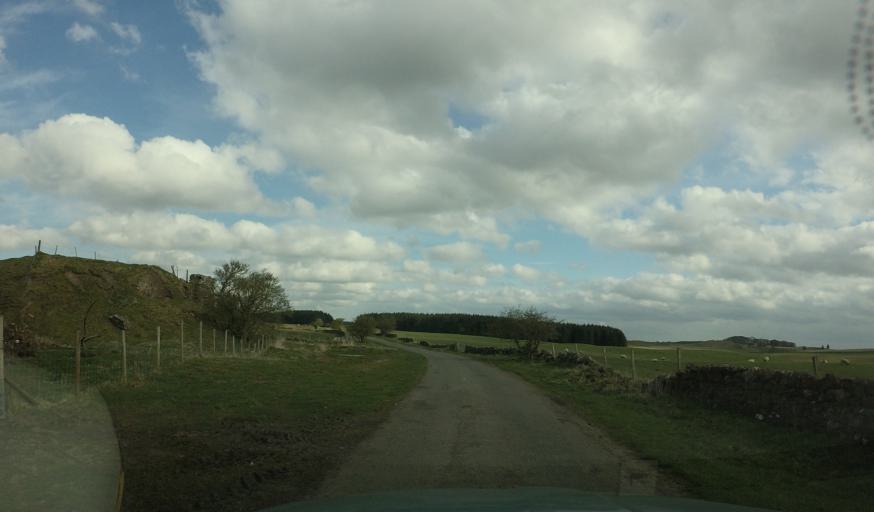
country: GB
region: Scotland
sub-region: Midlothian
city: Penicuik
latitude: 55.7916
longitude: -3.1666
